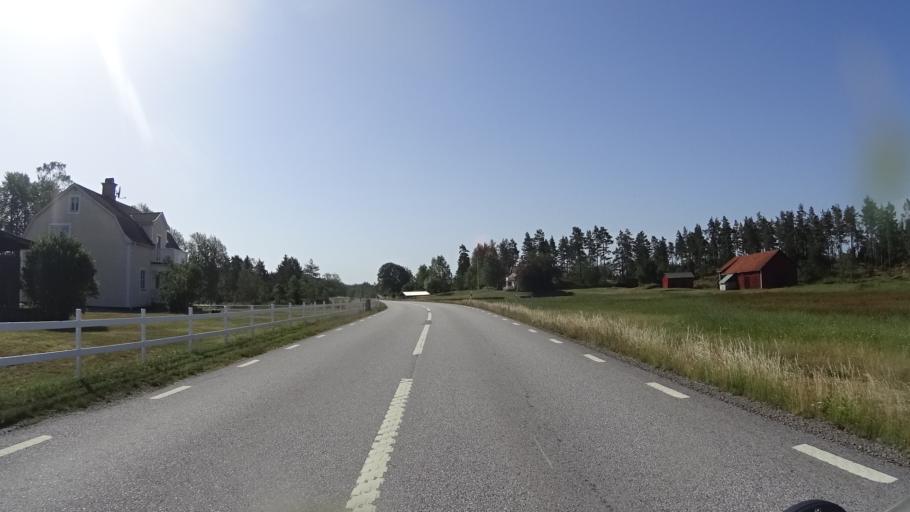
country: SE
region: OEstergoetland
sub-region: Atvidabergs Kommun
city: Atvidaberg
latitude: 58.0867
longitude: 16.1424
